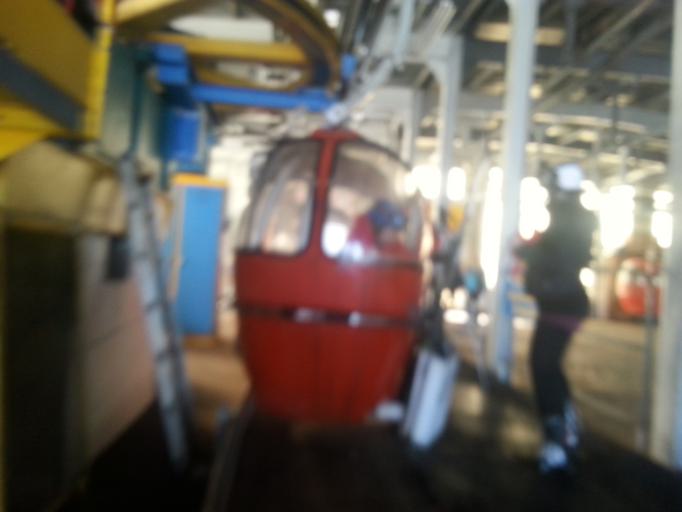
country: FR
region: Rhone-Alpes
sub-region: Departement de la Haute-Savoie
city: Samoens
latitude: 46.0537
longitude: 6.6986
